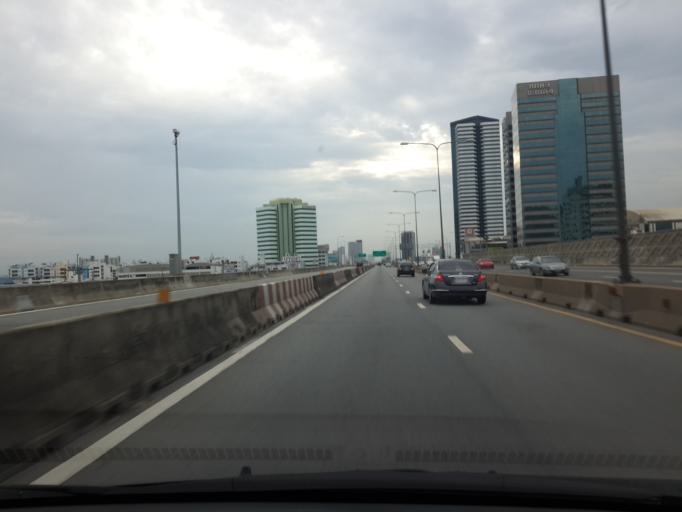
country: TH
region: Bangkok
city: Bang Na
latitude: 13.6668
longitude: 100.6392
